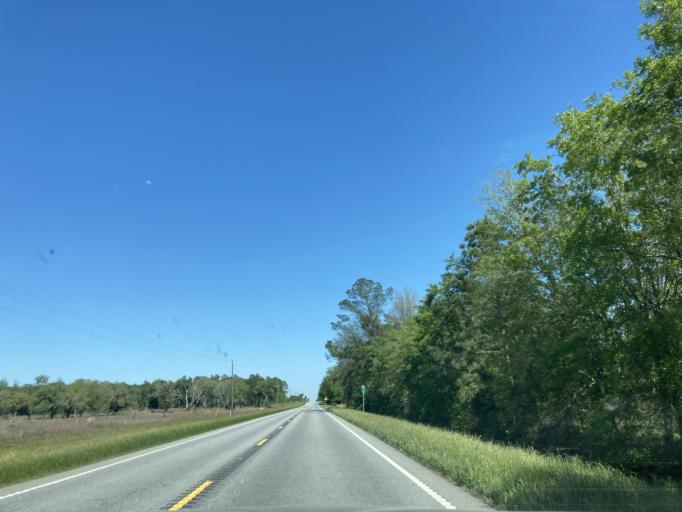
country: US
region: Georgia
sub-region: Miller County
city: Colquitt
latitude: 31.1860
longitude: -84.6210
